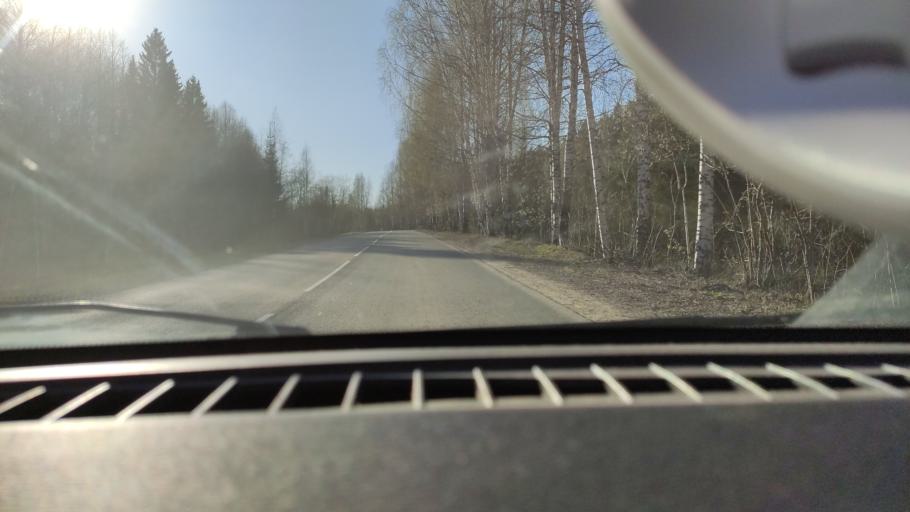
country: RU
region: Perm
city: Polazna
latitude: 58.1230
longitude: 56.4429
